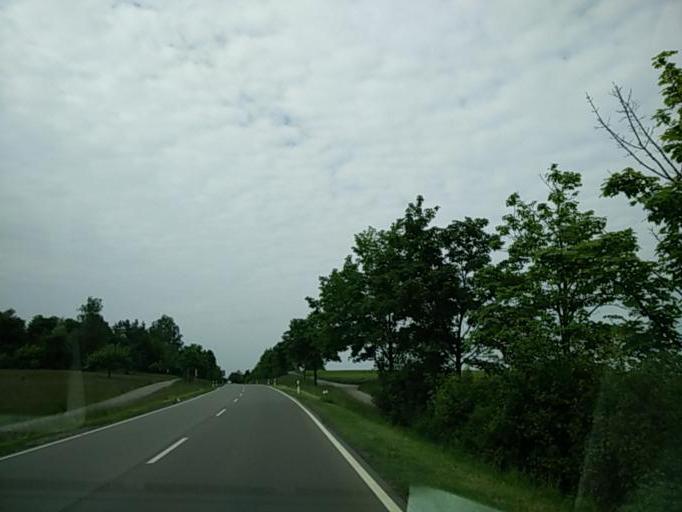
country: DE
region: Baden-Wuerttemberg
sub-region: Tuebingen Region
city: Rottenburg
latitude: 48.4549
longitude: 8.9220
